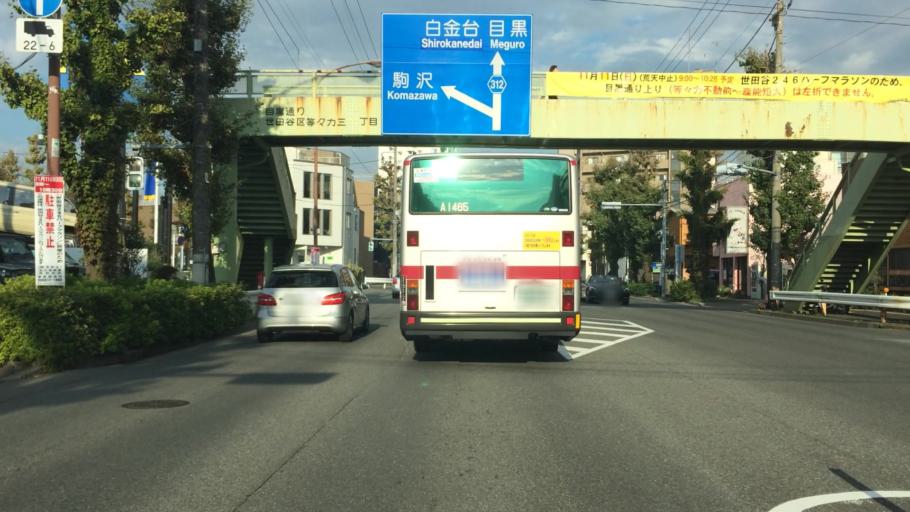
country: JP
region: Tokyo
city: Tokyo
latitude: 35.6110
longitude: 139.6521
